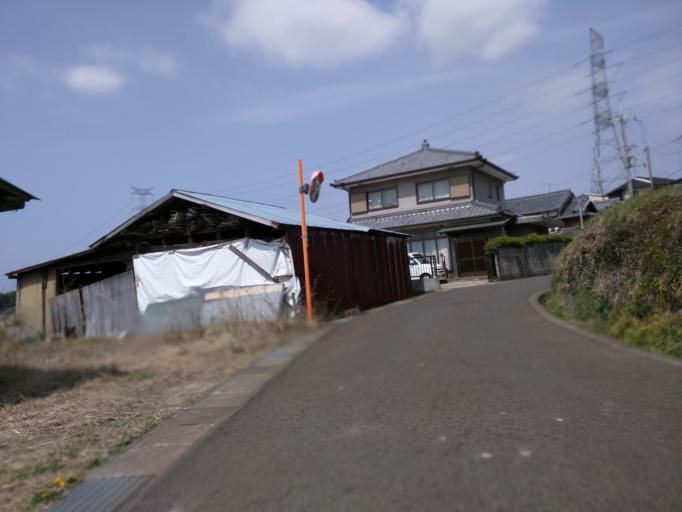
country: JP
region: Kyoto
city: Tanabe
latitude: 34.8031
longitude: 135.8161
